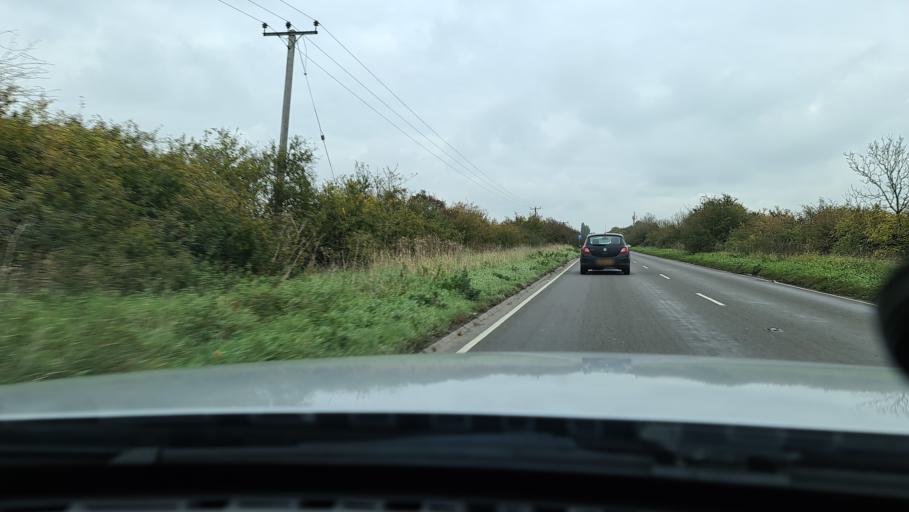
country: GB
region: England
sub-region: Oxfordshire
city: Bicester
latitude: 51.8740
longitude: -1.0666
